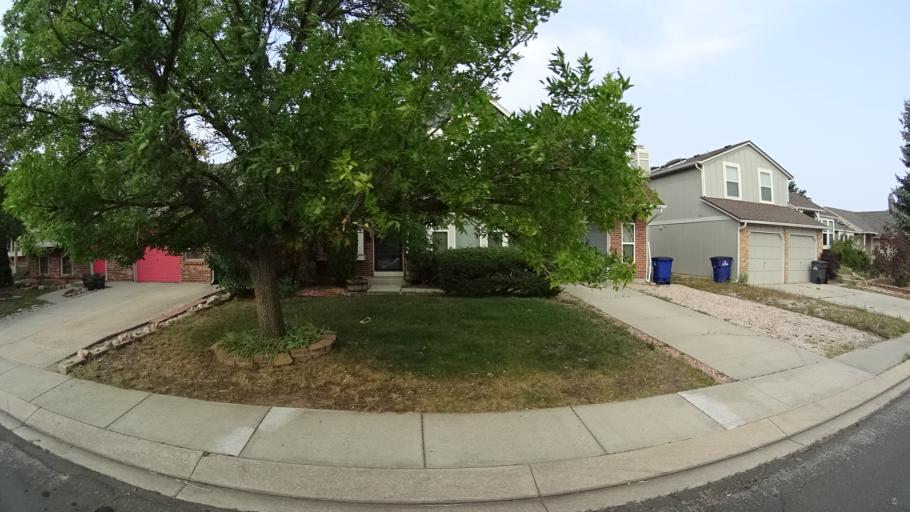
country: US
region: Colorado
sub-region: El Paso County
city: Stratmoor
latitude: 38.8058
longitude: -104.7500
